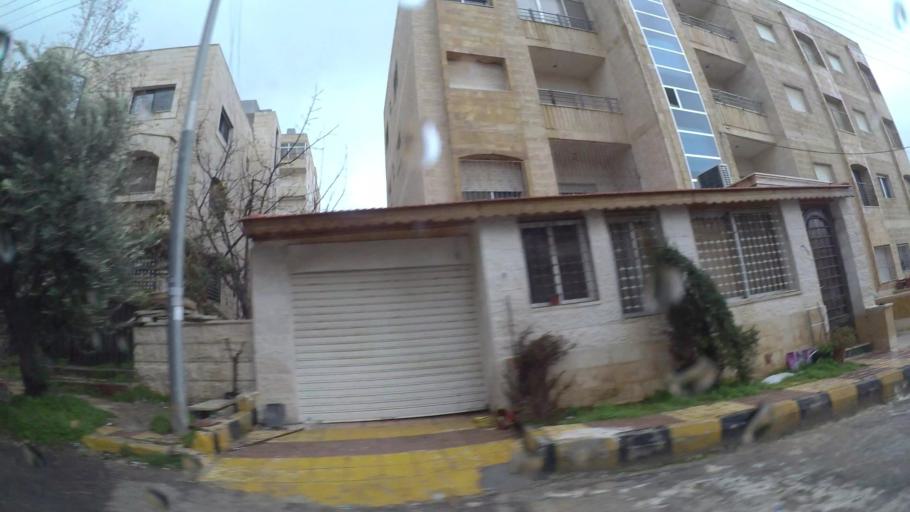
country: JO
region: Amman
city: Al Jubayhah
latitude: 32.0350
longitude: 35.8742
